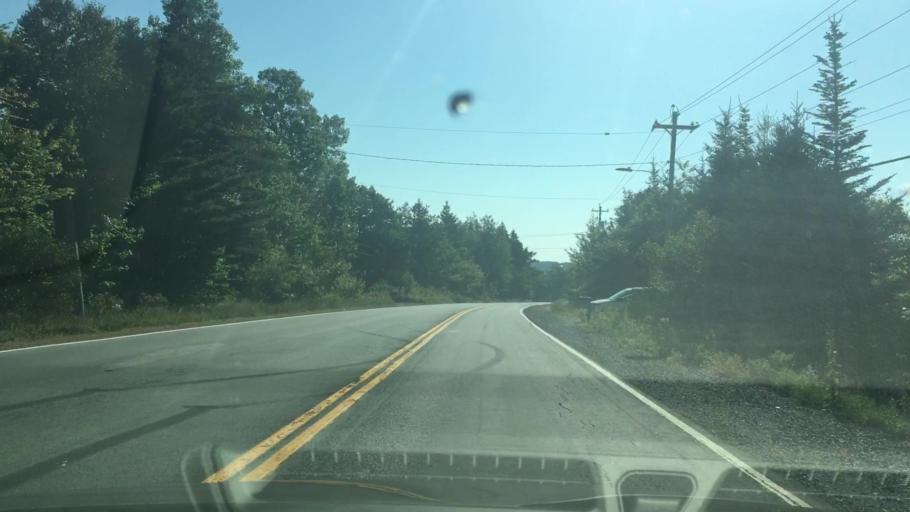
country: CA
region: Nova Scotia
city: Cole Harbour
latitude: 44.7779
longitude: -63.0749
